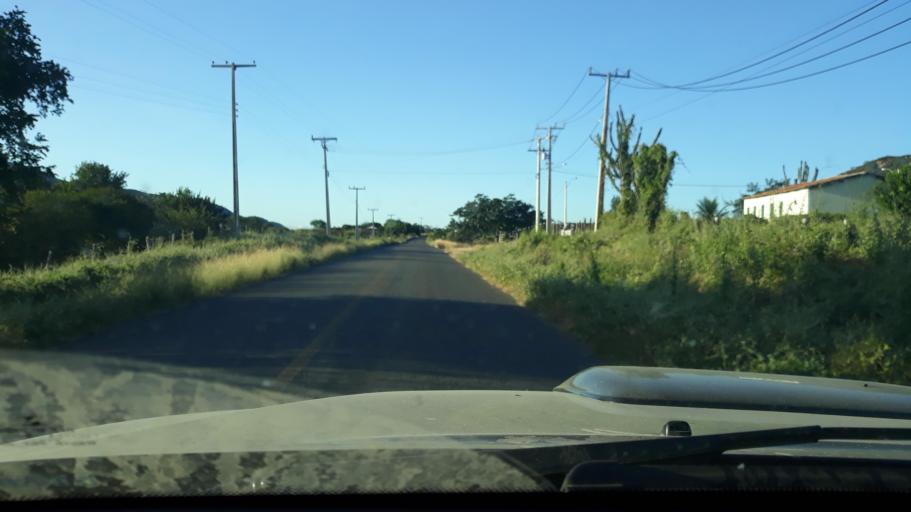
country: BR
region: Bahia
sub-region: Guanambi
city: Guanambi
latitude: -14.0448
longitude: -42.8735
